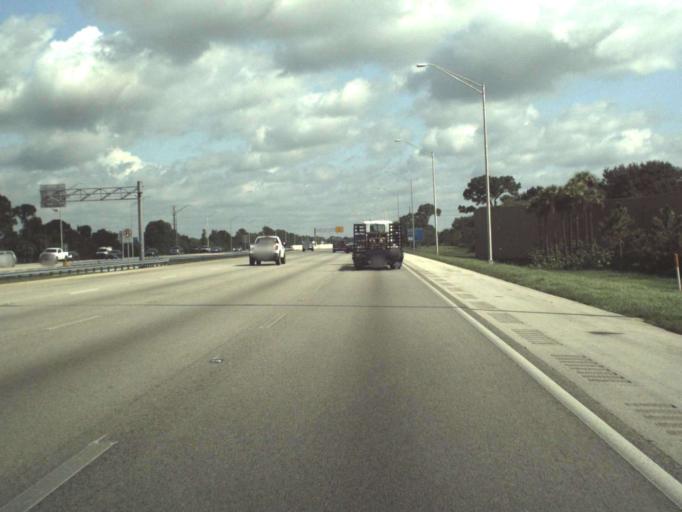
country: US
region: Florida
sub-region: Palm Beach County
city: Limestone Creek
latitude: 26.9065
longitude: -80.1400
